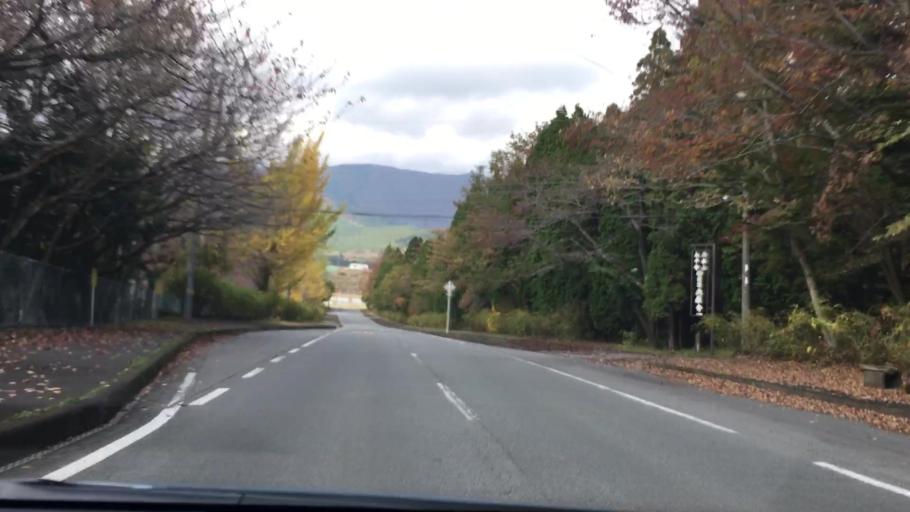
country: JP
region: Shizuoka
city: Gotemba
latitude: 35.3649
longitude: 138.9405
